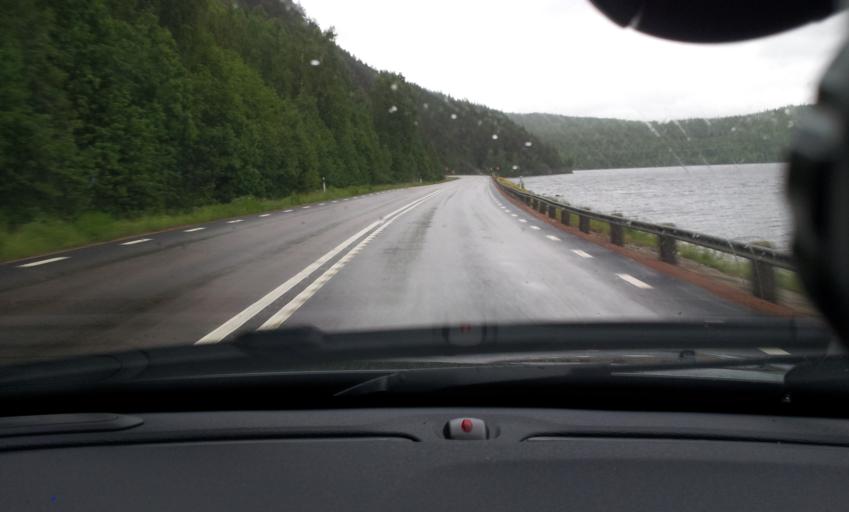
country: SE
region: Jaemtland
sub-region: Ragunda Kommun
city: Hammarstrand
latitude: 63.1398
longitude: 16.0197
